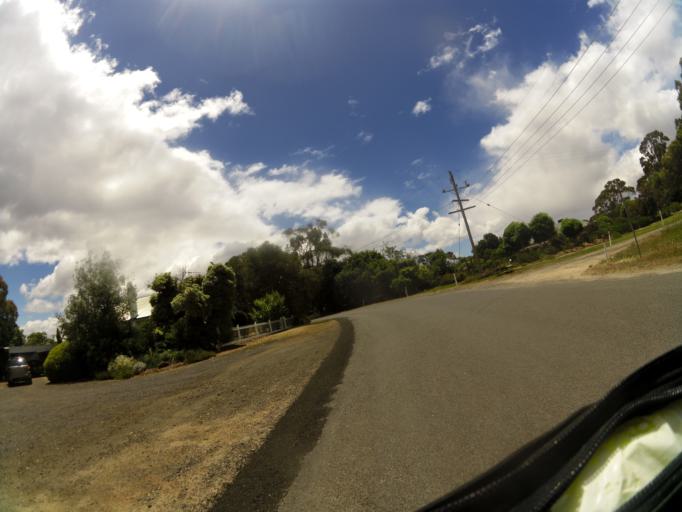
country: AU
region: Victoria
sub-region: Mount Alexander
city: Castlemaine
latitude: -37.0167
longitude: 144.2528
